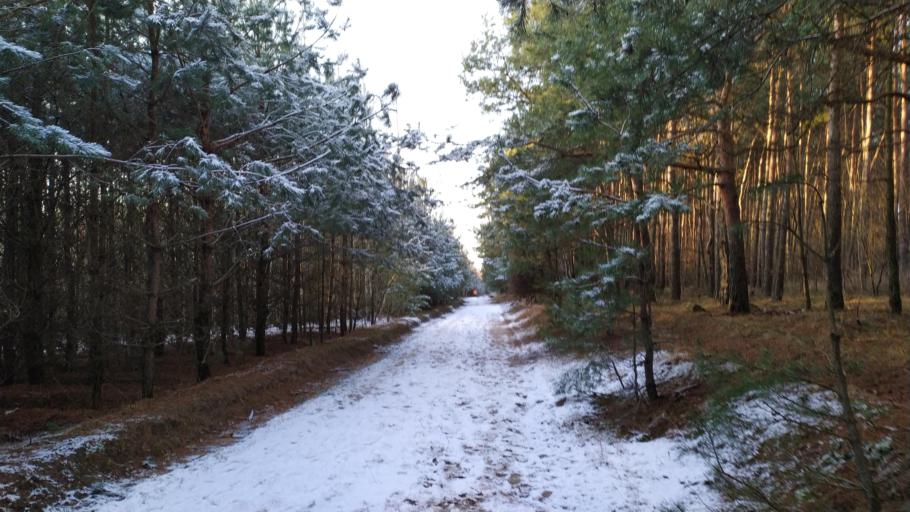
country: BY
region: Brest
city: Kamyanyets
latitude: 52.3825
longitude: 23.8342
